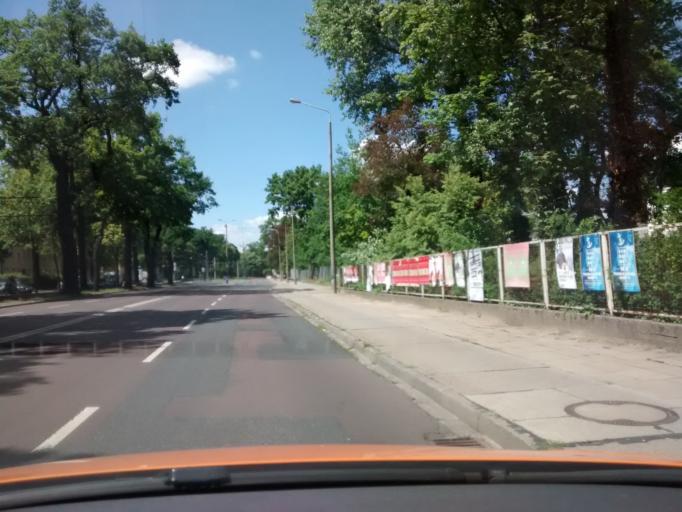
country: DE
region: Brandenburg
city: Potsdam
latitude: 52.3816
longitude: 13.0772
